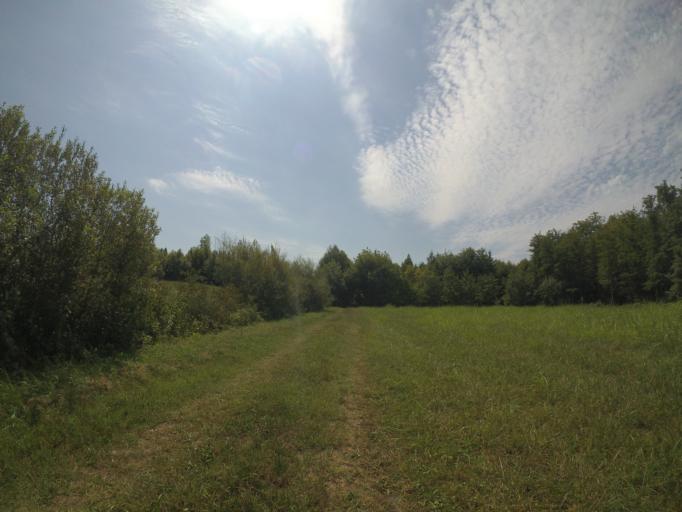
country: IT
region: Friuli Venezia Giulia
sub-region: Provincia di Udine
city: Bertiolo
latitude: 45.9269
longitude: 13.0628
